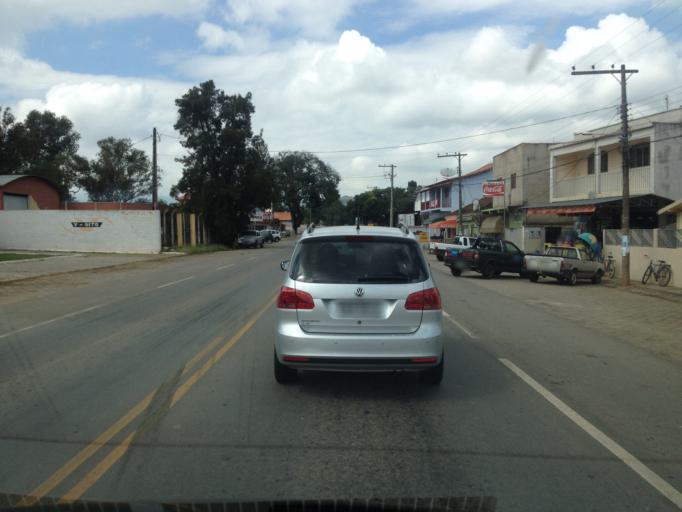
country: BR
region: Minas Gerais
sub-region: Itanhandu
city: Itanhandu
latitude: -22.2514
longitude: -44.9341
